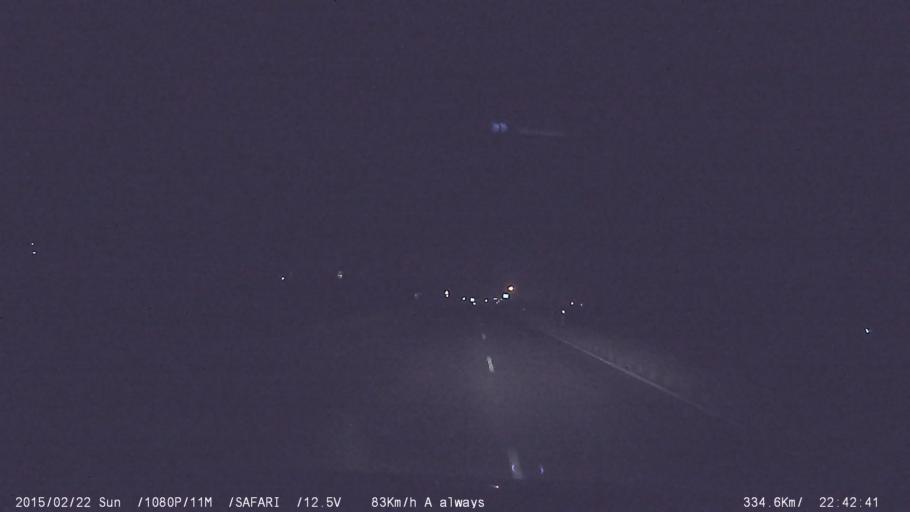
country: IN
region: Tamil Nadu
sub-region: Namakkal
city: Namakkal
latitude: 11.1894
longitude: 78.0850
